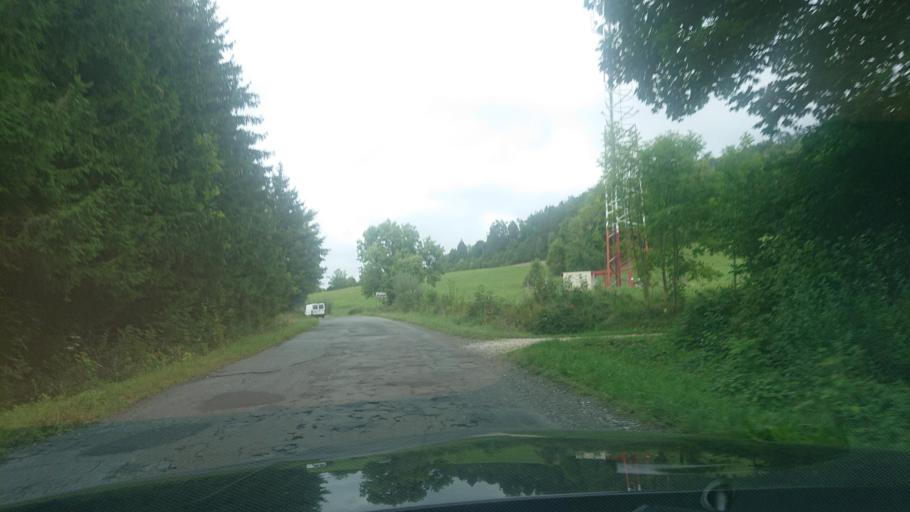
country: PL
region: Lower Silesian Voivodeship
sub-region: Powiat klodzki
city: Bystrzyca Klodzka
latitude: 50.3139
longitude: 16.7361
